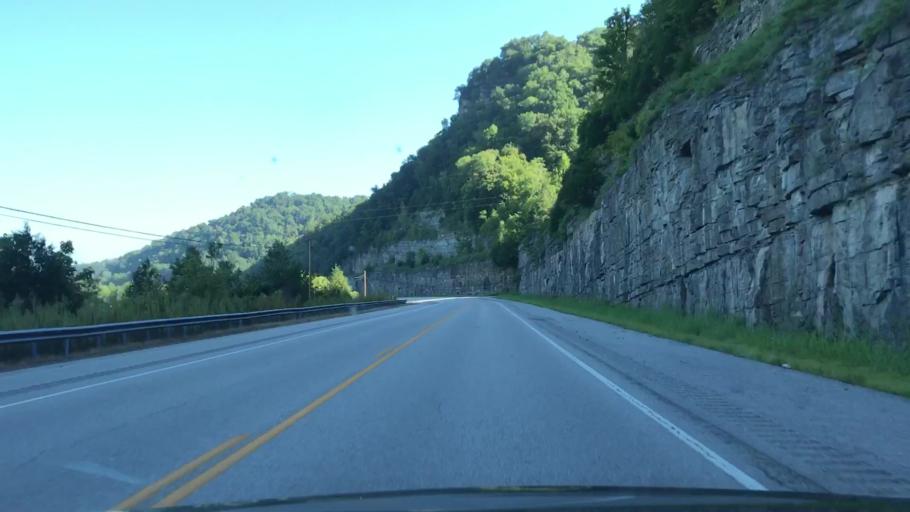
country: US
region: Tennessee
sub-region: Clay County
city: Celina
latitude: 36.4577
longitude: -85.5762
